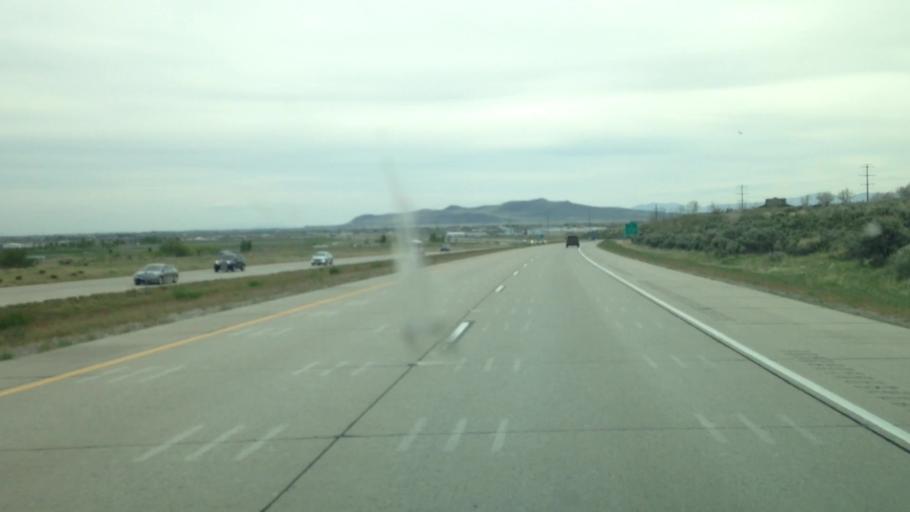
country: US
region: Utah
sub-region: Box Elder County
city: Garland
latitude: 41.7404
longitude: -112.1896
